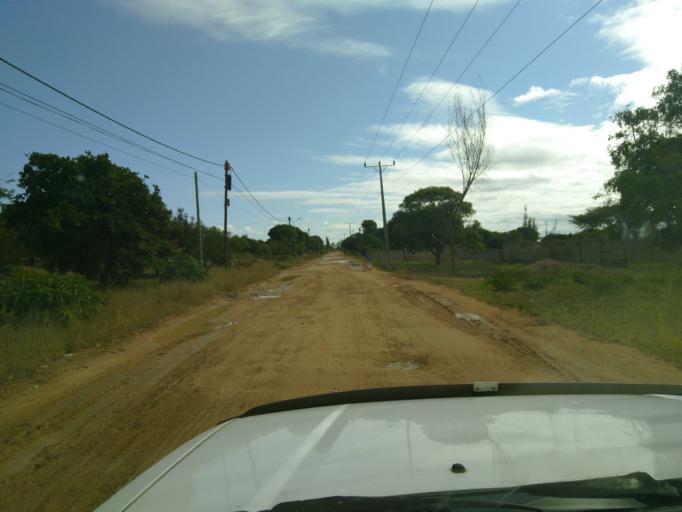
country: MZ
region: Maputo City
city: Maputo
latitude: -25.9978
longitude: 32.5399
